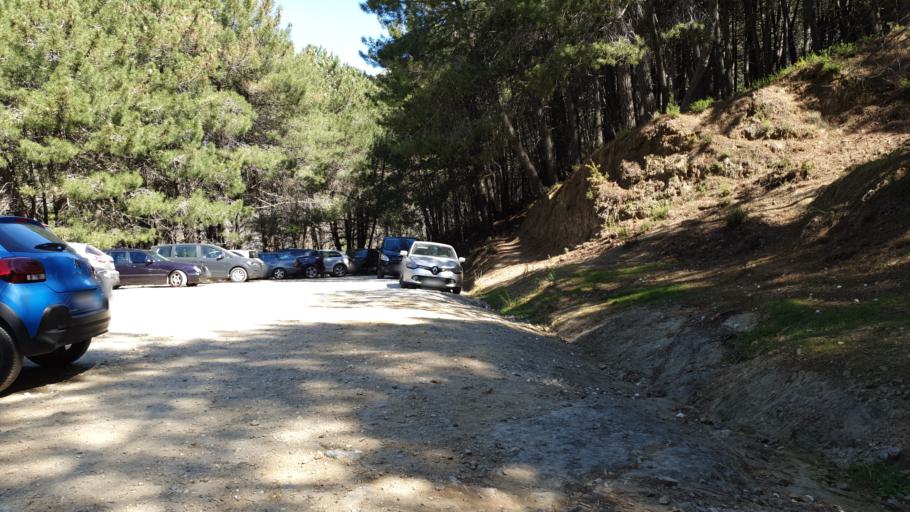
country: ES
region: Andalusia
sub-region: Provincia de Malaga
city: Ojen
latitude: 36.5766
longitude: -4.8846
